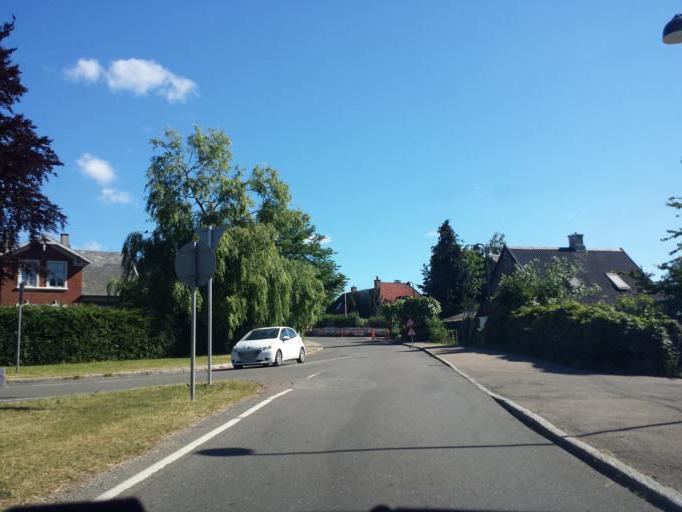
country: DK
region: Capital Region
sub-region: Egedal Kommune
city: Ganlose
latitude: 55.7938
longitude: 12.2628
